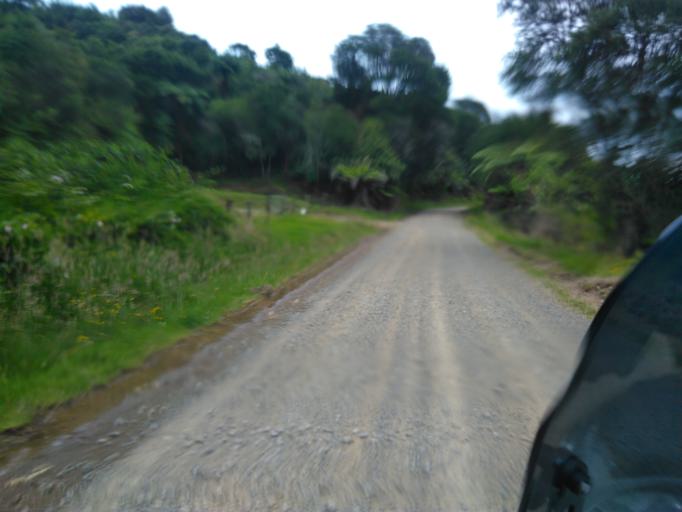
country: NZ
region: Bay of Plenty
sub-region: Opotiki District
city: Opotiki
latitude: -38.0267
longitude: 177.4393
